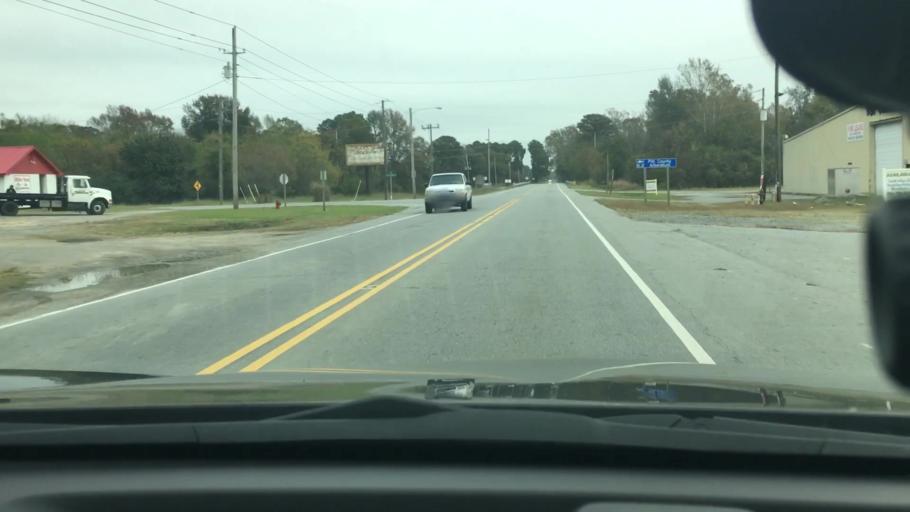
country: US
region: North Carolina
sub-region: Pitt County
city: Greenville
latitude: 35.6349
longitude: -77.3657
